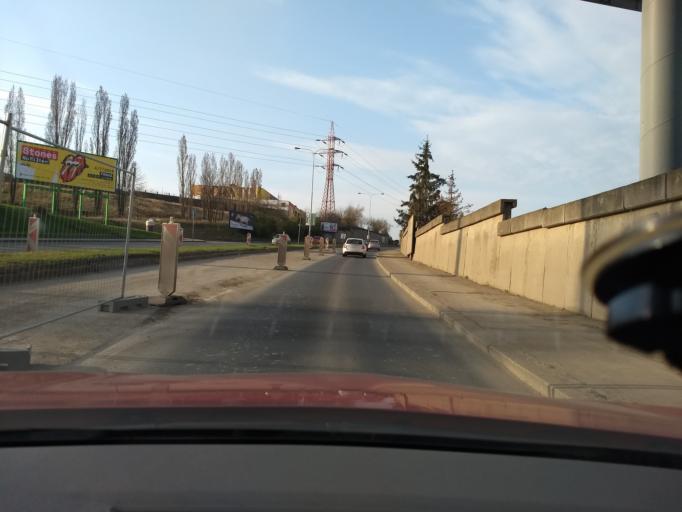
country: CZ
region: Central Bohemia
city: Hostivice
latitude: 50.0580
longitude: 14.3112
